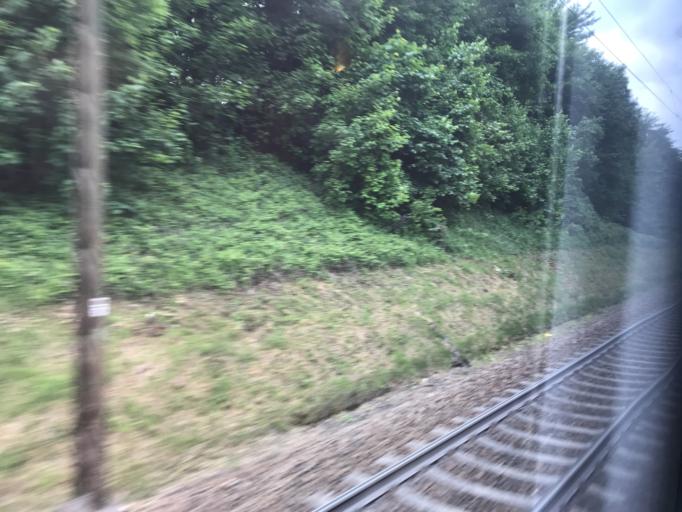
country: DE
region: Baden-Wuerttemberg
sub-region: Tuebingen Region
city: Amstetten
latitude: 48.5851
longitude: 9.8683
